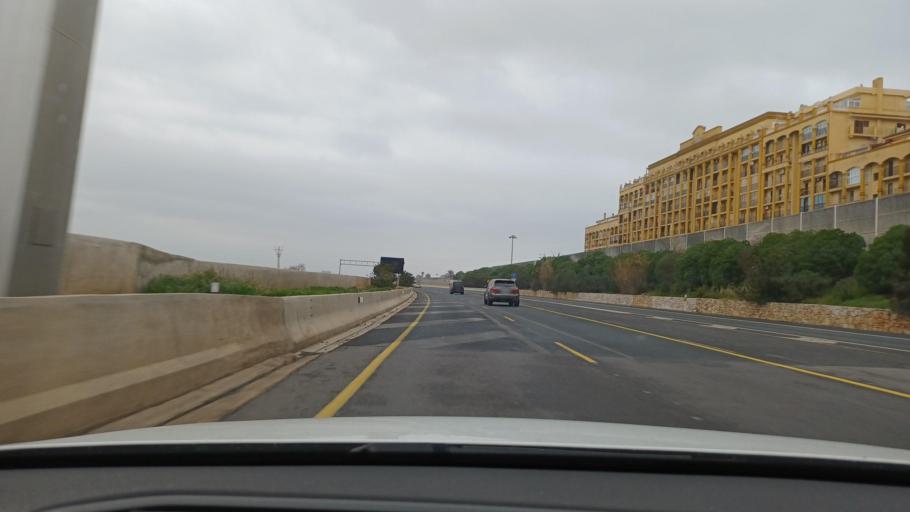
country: ES
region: Valencia
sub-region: Provincia de Valencia
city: Meliana
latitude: 39.5131
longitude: -0.3221
